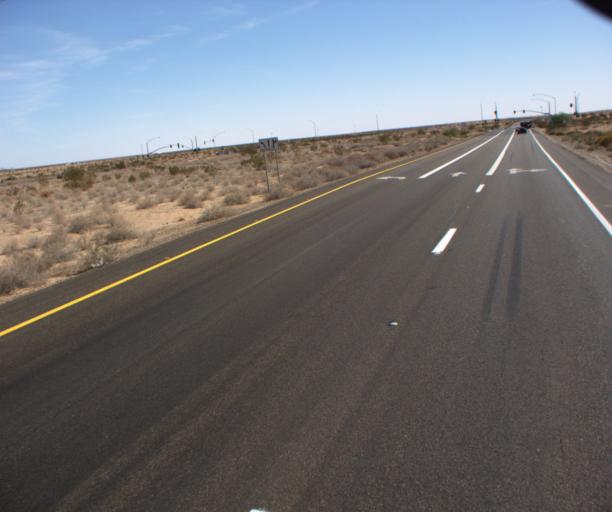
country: US
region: Arizona
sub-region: Yuma County
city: Fortuna Foothills
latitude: 32.6287
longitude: -114.5215
